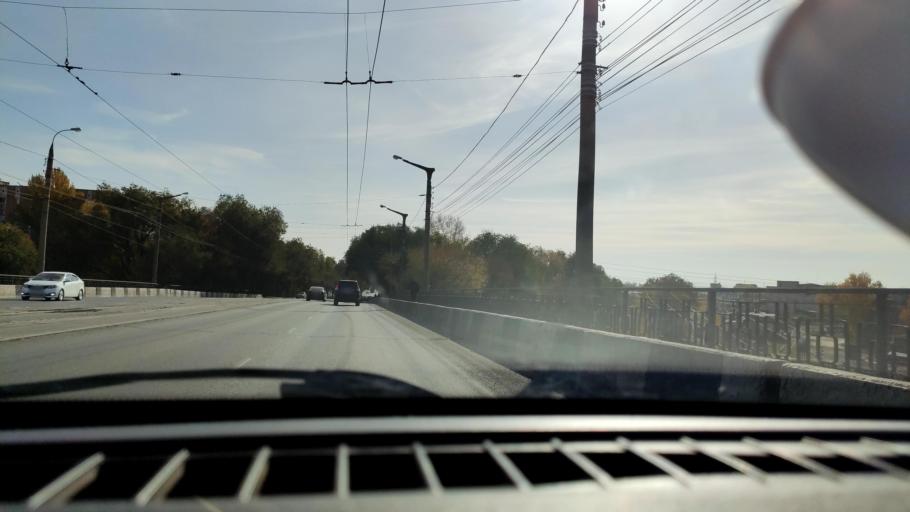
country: RU
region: Samara
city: Samara
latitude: 53.2008
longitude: 50.2426
